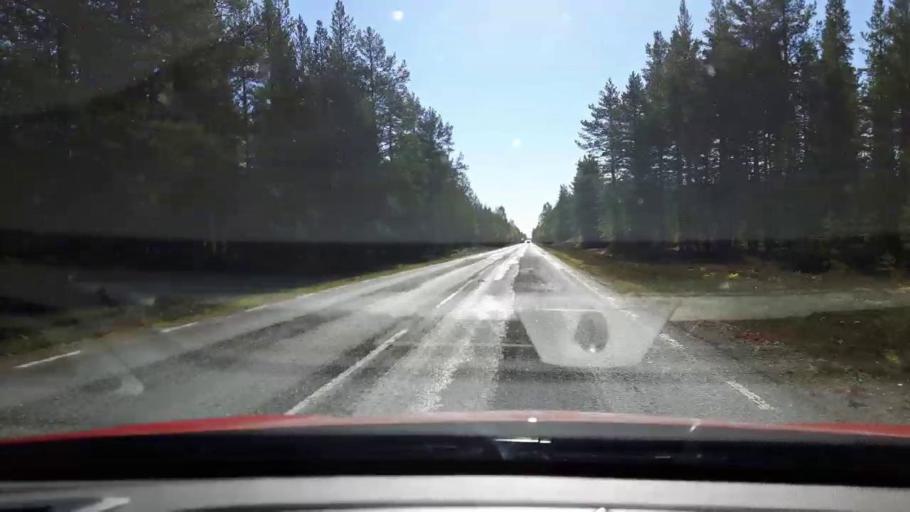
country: SE
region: Jaemtland
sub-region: Harjedalens Kommun
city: Sveg
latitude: 62.4213
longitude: 13.9071
